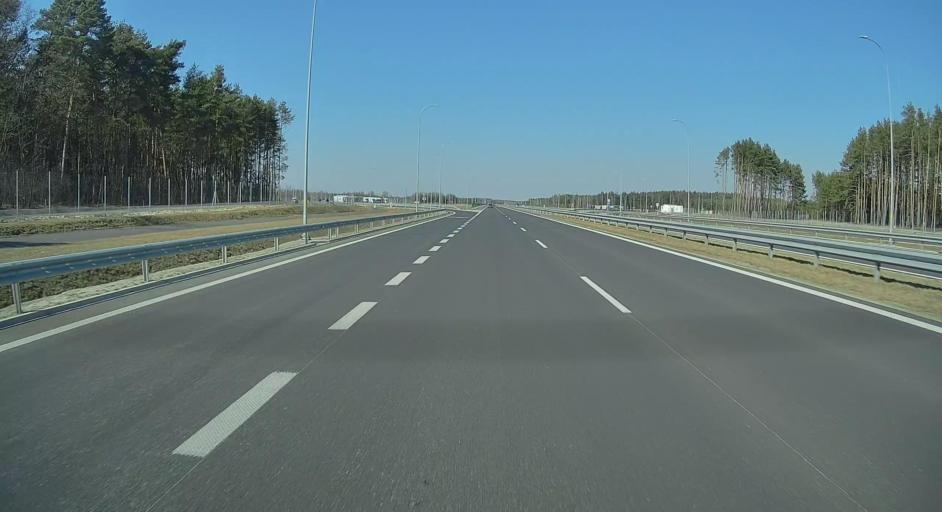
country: PL
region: Subcarpathian Voivodeship
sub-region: Powiat nizanski
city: Jezowe
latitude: 50.3849
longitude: 22.1619
